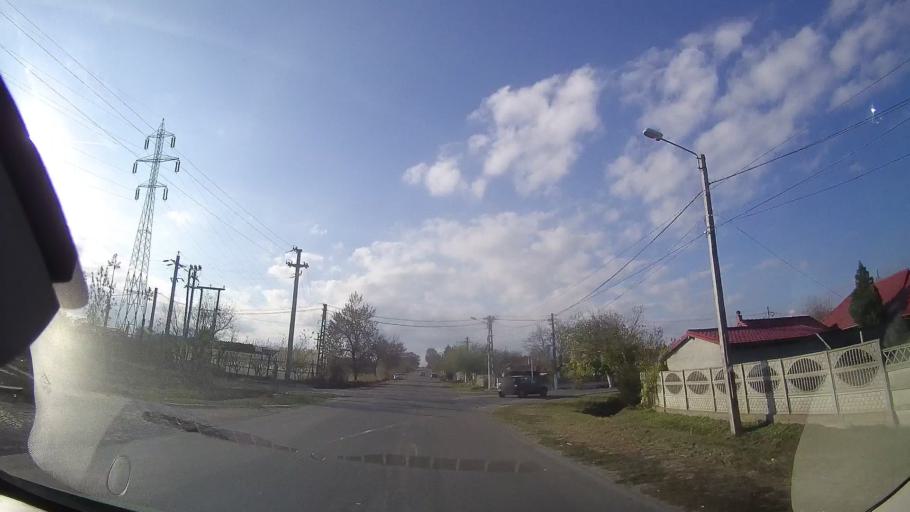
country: RO
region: Constanta
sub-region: Comuna Limanu
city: Limanu
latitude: 43.7941
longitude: 28.5334
